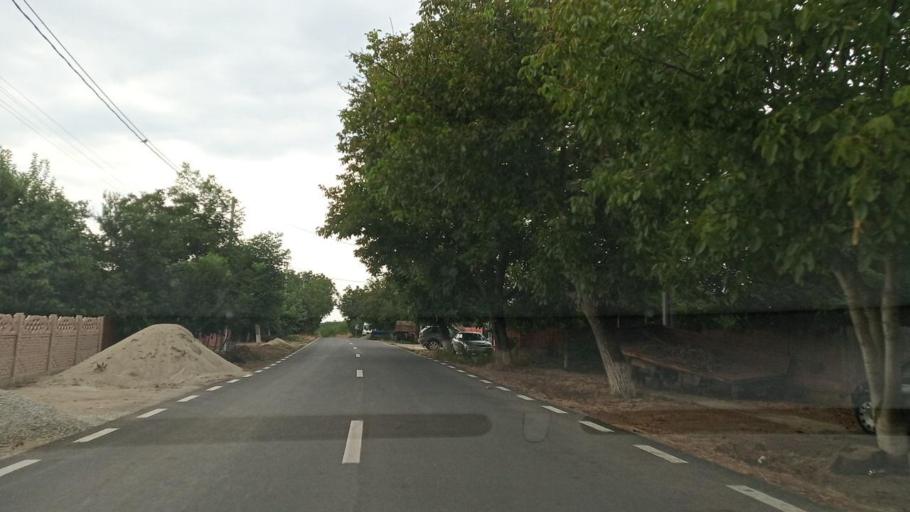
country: RO
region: Giurgiu
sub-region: Comuna Izvoarele
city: Isvoarele
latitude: 44.1685
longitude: 26.2753
